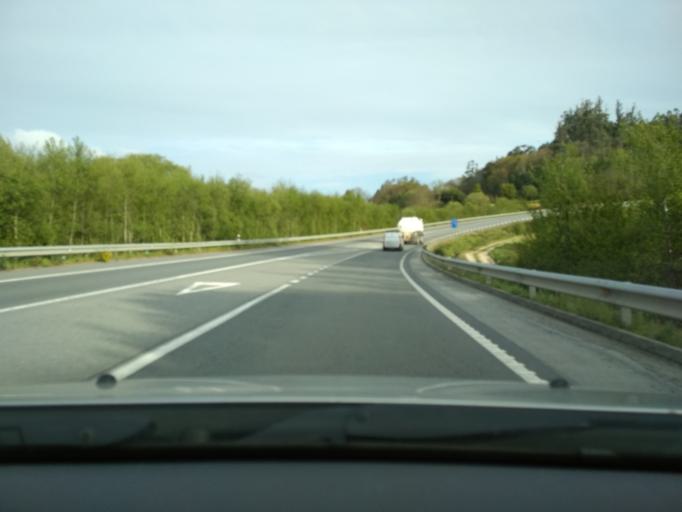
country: ES
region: Galicia
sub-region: Provincia da Coruna
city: Cerceda
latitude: 43.2182
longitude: -8.4565
